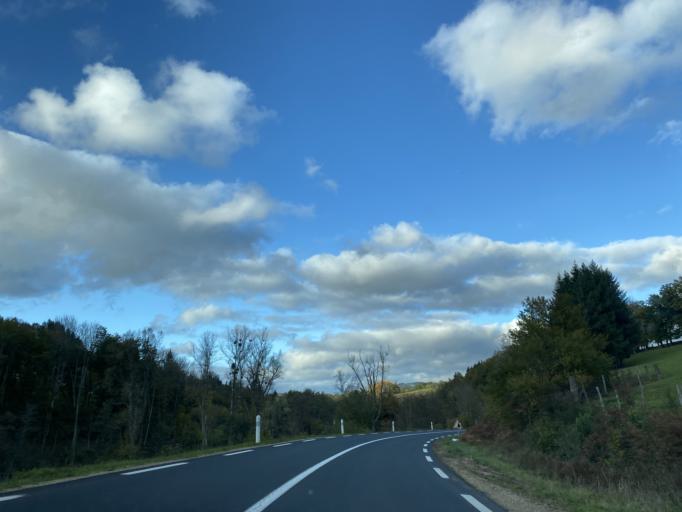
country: FR
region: Auvergne
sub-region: Departement du Puy-de-Dome
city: Job
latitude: 45.6470
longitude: 3.6660
